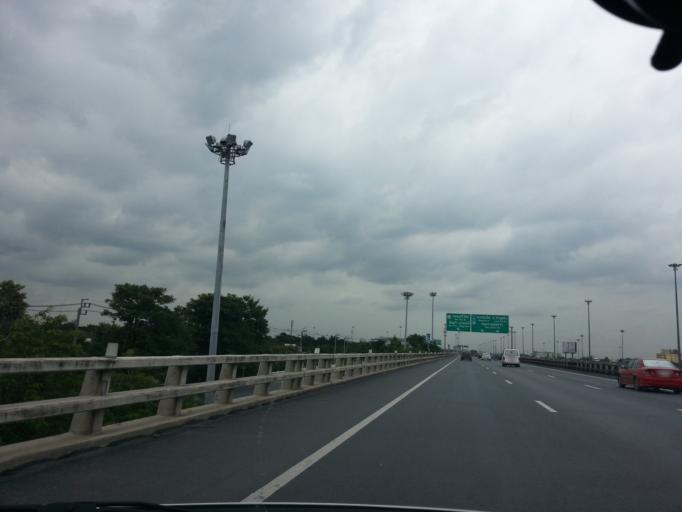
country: TH
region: Bangkok
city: Saphan Sung
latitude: 13.7848
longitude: 100.6845
